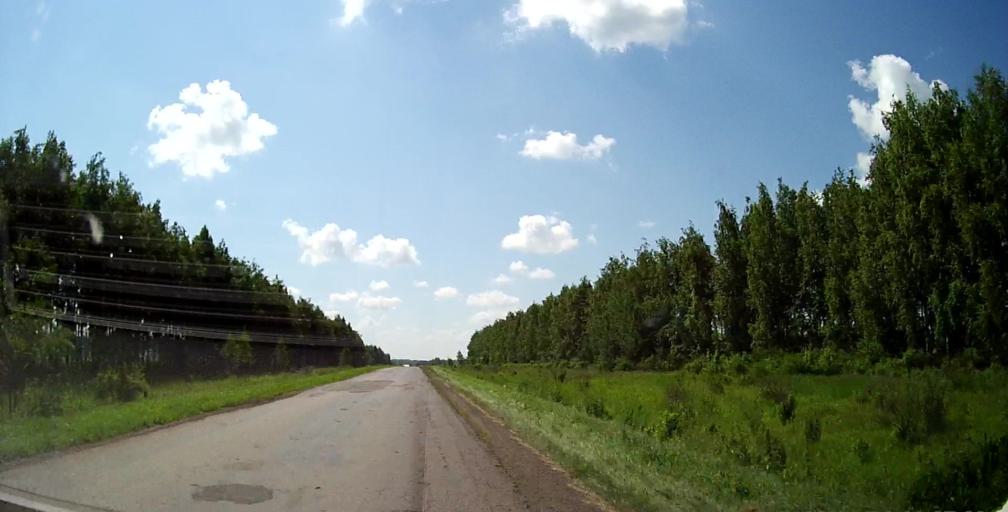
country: RU
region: Lipetsk
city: Chaplygin
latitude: 53.3624
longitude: 39.9197
